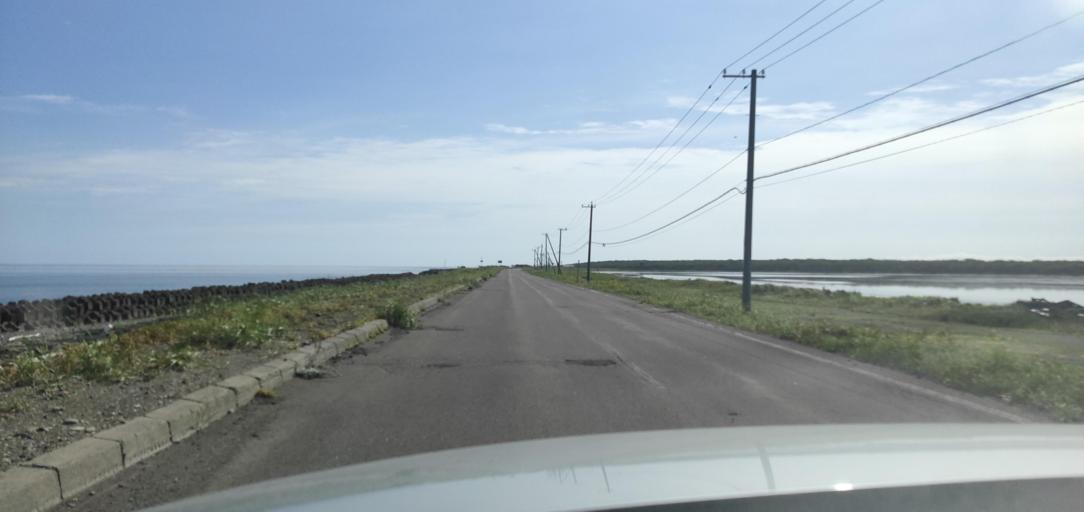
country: JP
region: Hokkaido
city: Shibetsu
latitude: 43.6126
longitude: 145.2586
